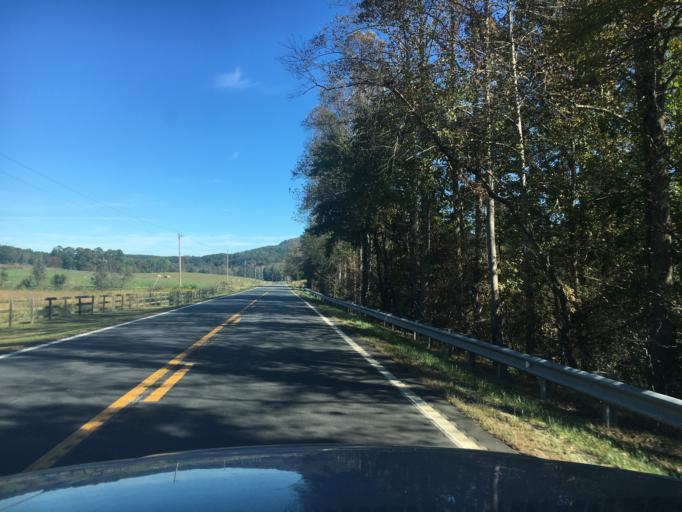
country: US
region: North Carolina
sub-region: Burke County
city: Glen Alpine
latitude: 35.5972
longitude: -81.8242
